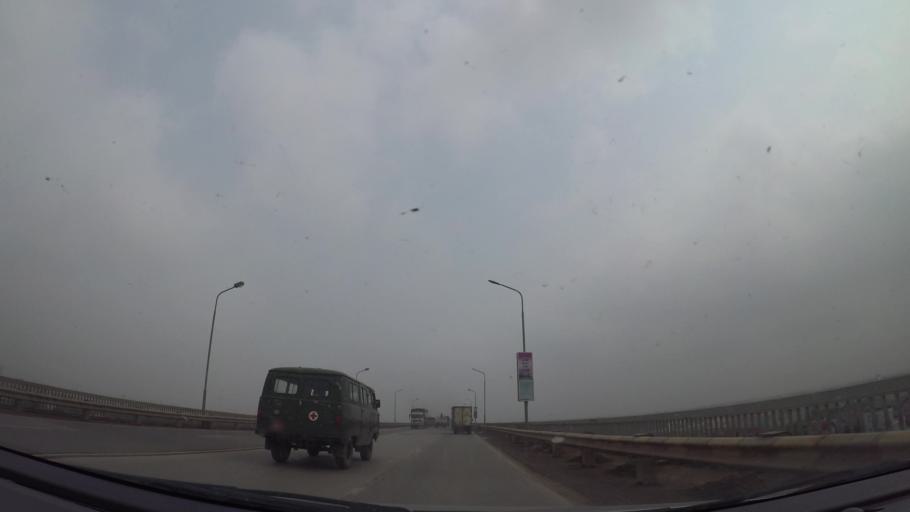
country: VN
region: Ha Noi
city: Tay Ho
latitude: 21.1022
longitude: 105.7867
